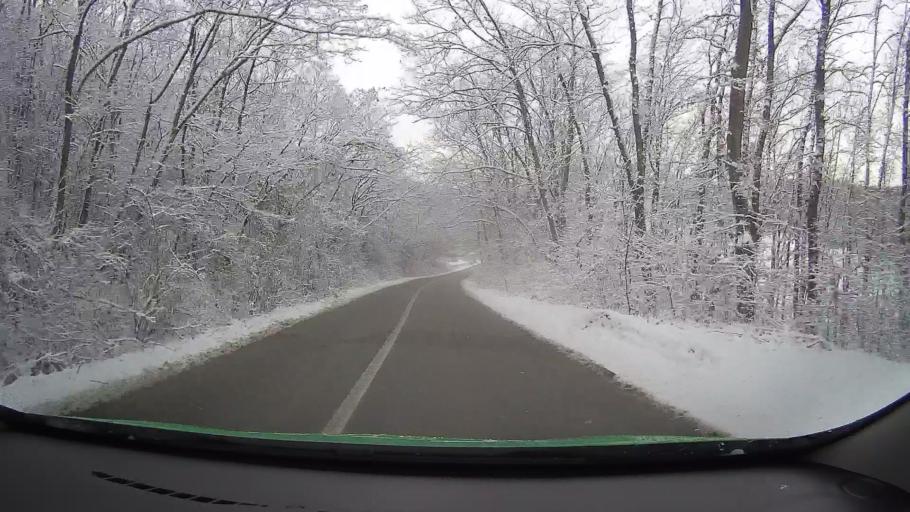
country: RO
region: Hunedoara
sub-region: Oras Hateg
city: Hateg
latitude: 45.6369
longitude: 22.9207
